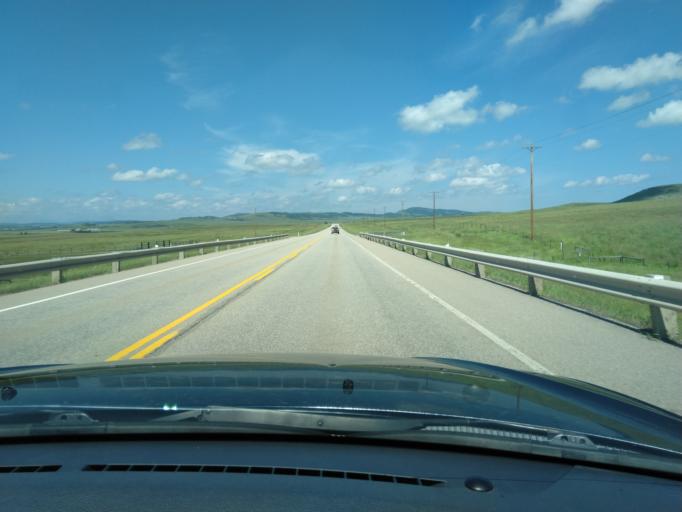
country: CA
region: Alberta
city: Cochrane
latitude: 51.2213
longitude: -114.5453
